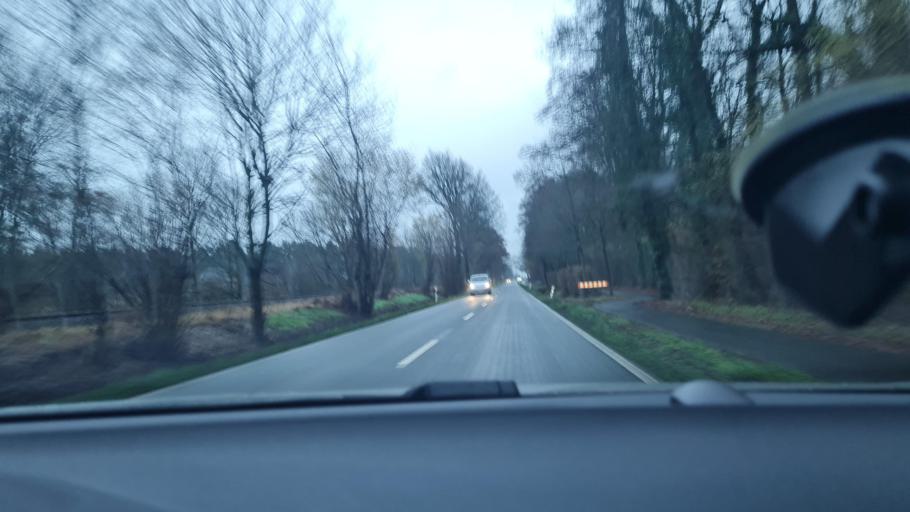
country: DE
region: North Rhine-Westphalia
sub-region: Regierungsbezirk Munster
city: Heiden
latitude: 51.8058
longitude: 6.9078
